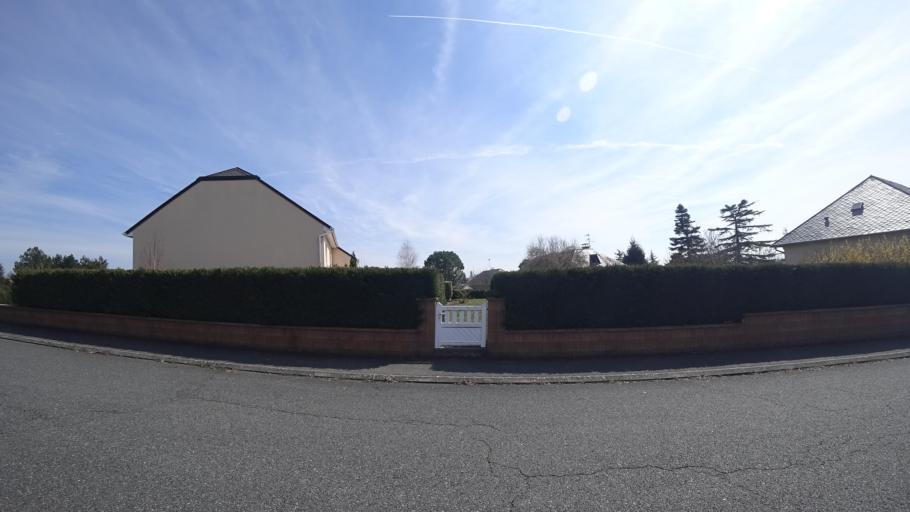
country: FR
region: Midi-Pyrenees
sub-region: Departement de l'Aveyron
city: Olemps
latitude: 44.3718
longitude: 2.5555
